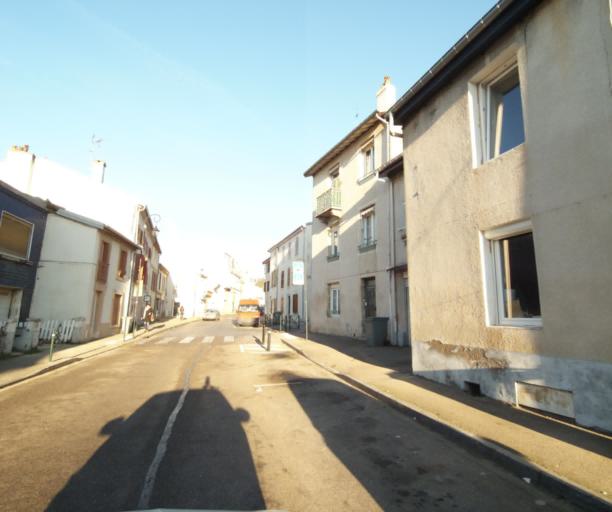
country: FR
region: Lorraine
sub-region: Departement de Meurthe-et-Moselle
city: Laxou
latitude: 48.6856
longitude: 6.1441
